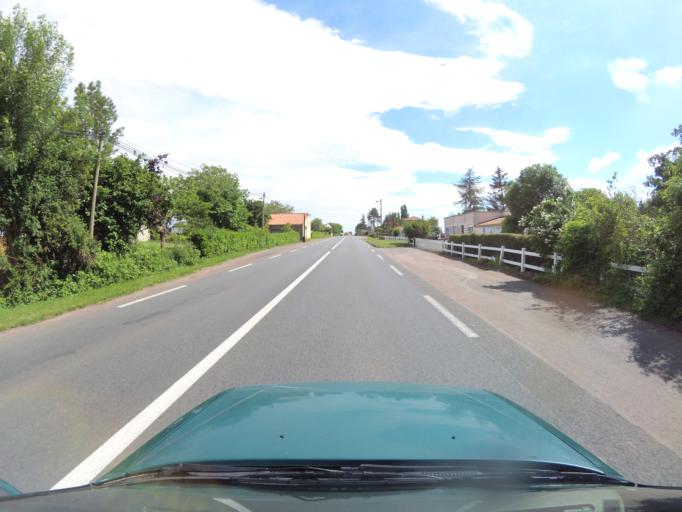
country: FR
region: Pays de la Loire
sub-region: Departement de la Vendee
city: Sainte-Hermine
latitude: 46.5992
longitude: -1.0385
